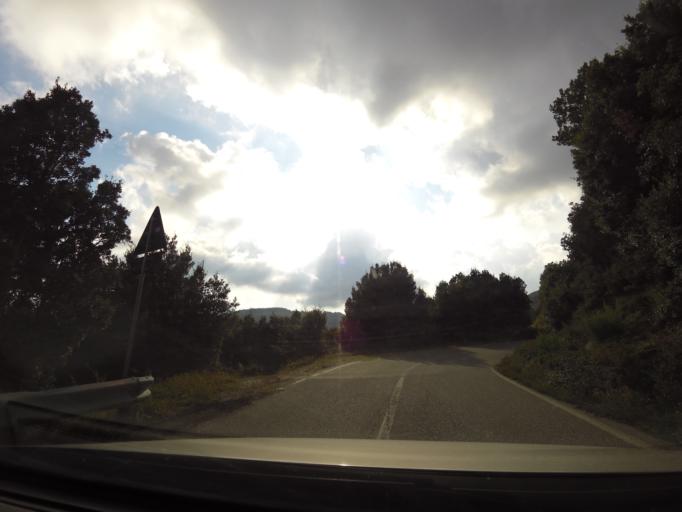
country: IT
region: Calabria
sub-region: Provincia di Vibo-Valentia
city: Nardodipace
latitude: 38.4770
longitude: 16.3849
